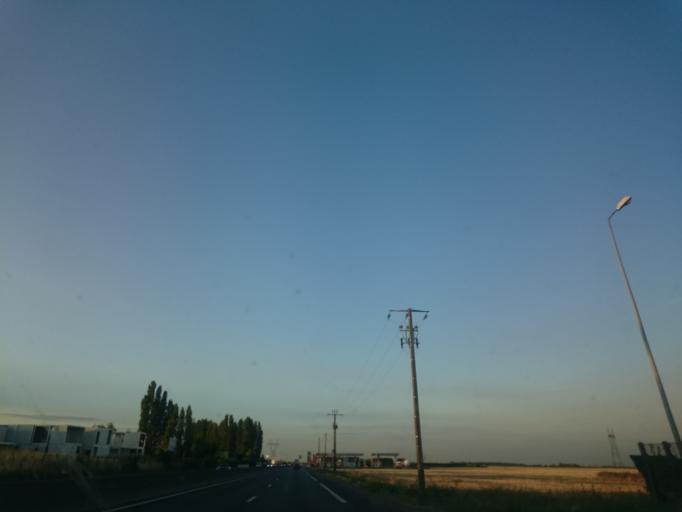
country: FR
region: Ile-de-France
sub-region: Departement de l'Essonne
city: Boissy-sous-Saint-Yon
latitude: 48.5611
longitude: 2.2267
